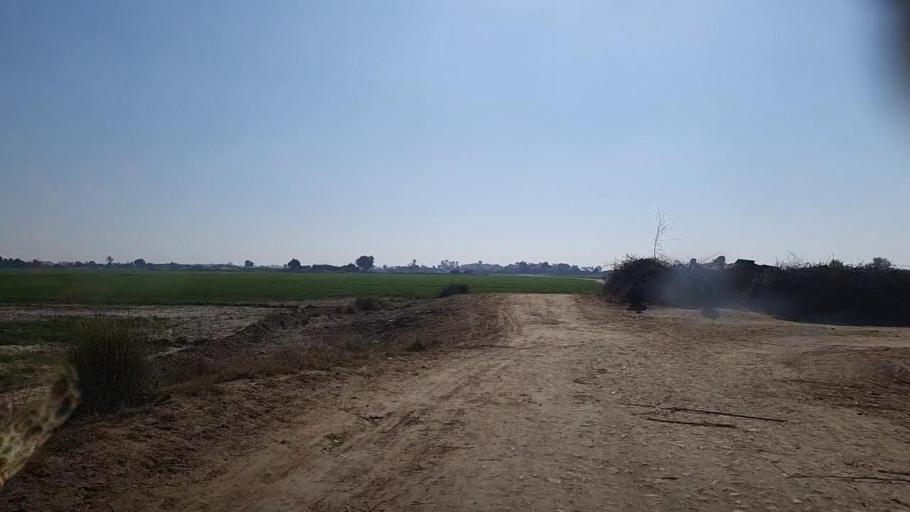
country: PK
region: Sindh
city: Khairpur
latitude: 28.0348
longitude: 69.7841
